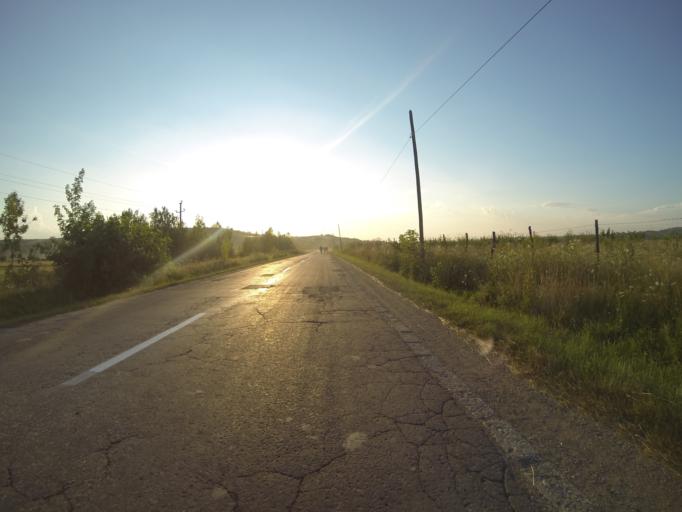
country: RO
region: Brasov
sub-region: Comuna Sinca Veche
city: Sinca Veche
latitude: 45.7483
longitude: 25.1881
